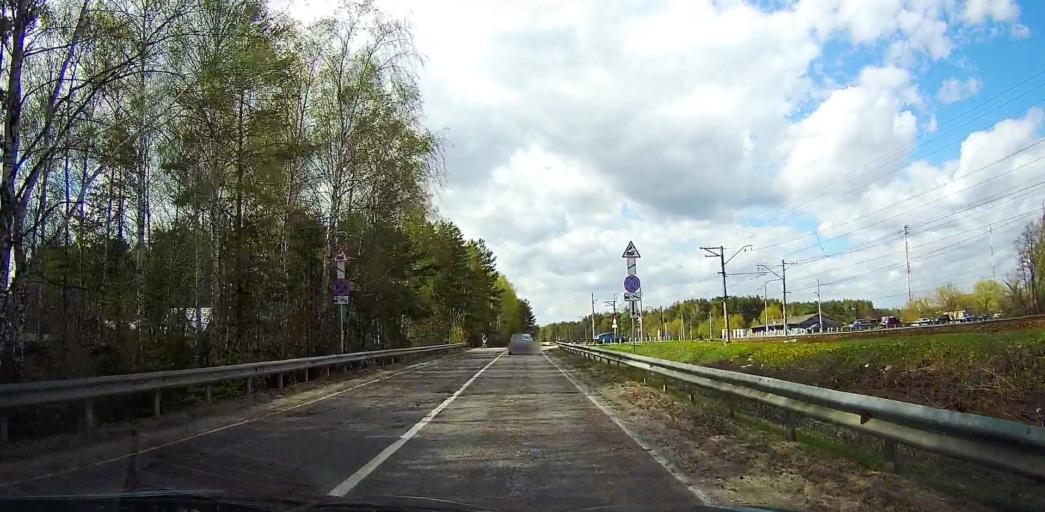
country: RU
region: Moskovskaya
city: Davydovo
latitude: 55.5726
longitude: 38.8200
